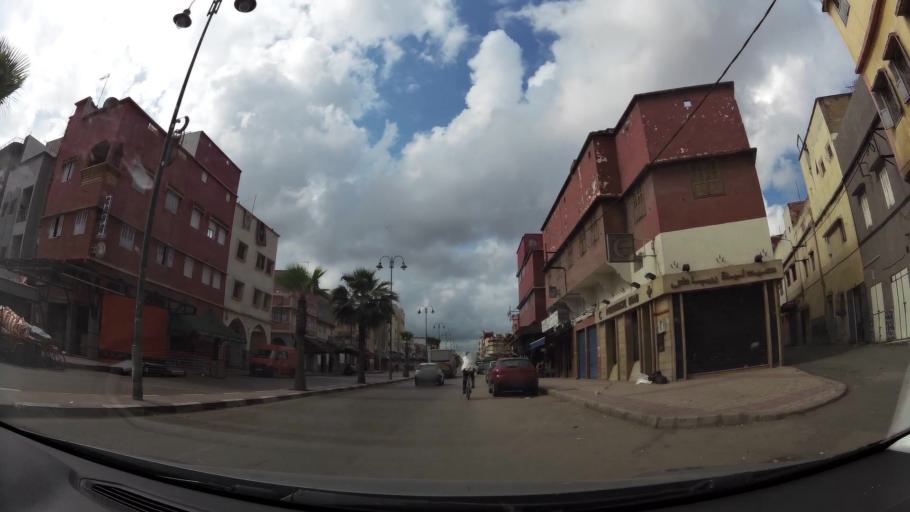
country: MA
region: Gharb-Chrarda-Beni Hssen
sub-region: Kenitra Province
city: Kenitra
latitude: 34.2657
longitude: -6.5616
